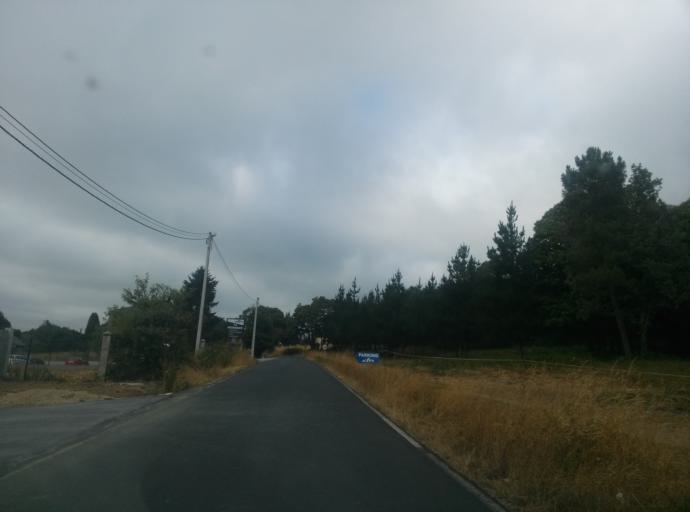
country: ES
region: Galicia
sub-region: Provincia de Lugo
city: Mos
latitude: 43.0868
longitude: -7.5465
